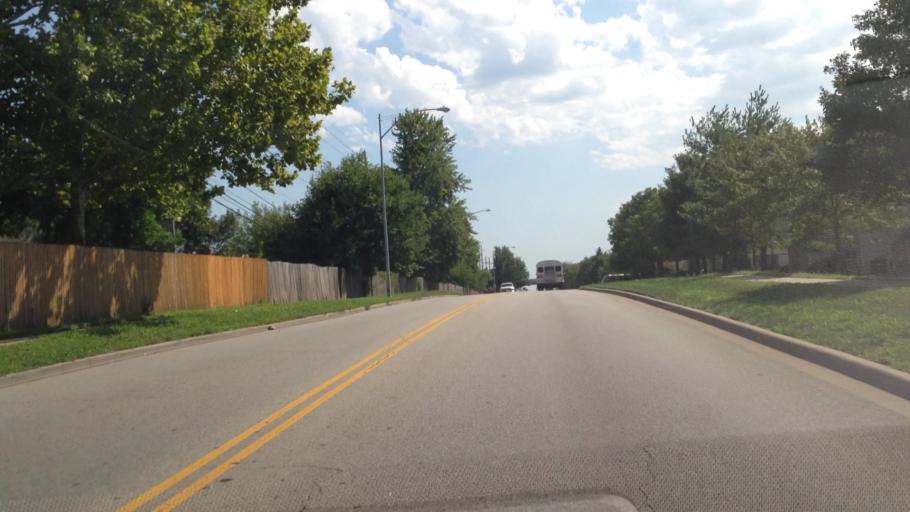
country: US
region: Kansas
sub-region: Johnson County
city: Lenexa
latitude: 38.9410
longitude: -94.7422
